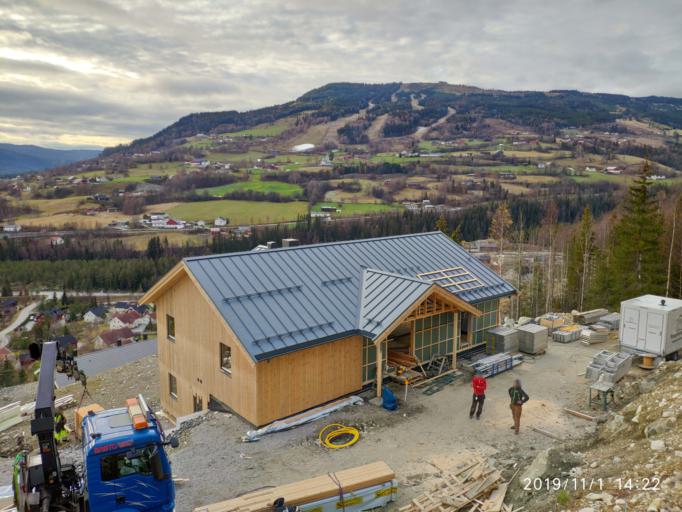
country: NO
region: Buskerud
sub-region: Gol
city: Gol
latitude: 60.7120
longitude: 8.9376
